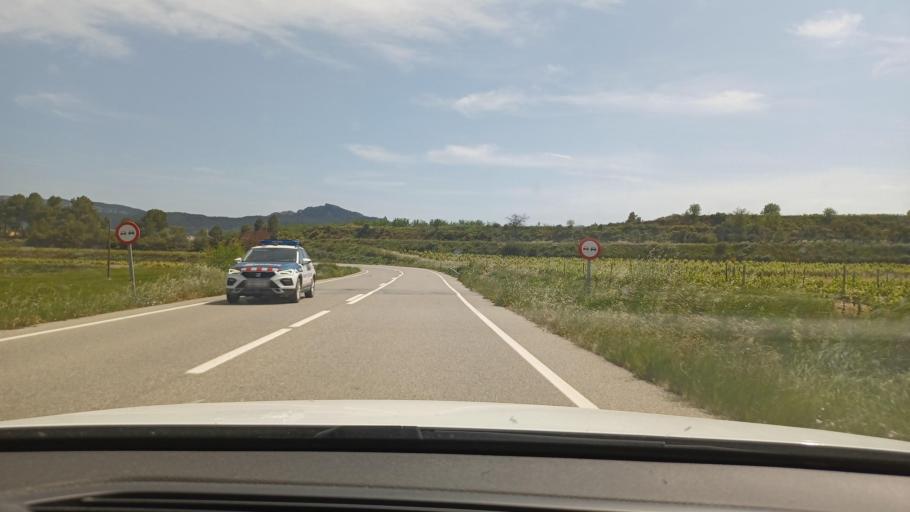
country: ES
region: Catalonia
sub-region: Provincia de Tarragona
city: Gandesa
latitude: 41.0699
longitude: 0.4307
